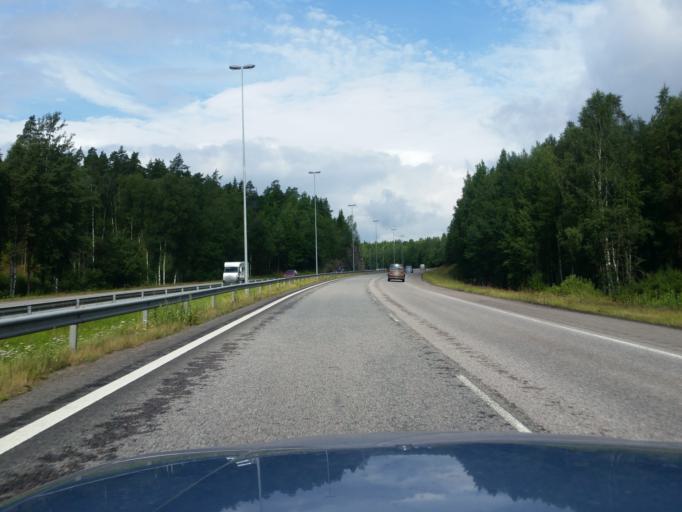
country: FI
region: Uusimaa
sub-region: Helsinki
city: Kirkkonummi
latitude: 60.2858
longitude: 24.4202
